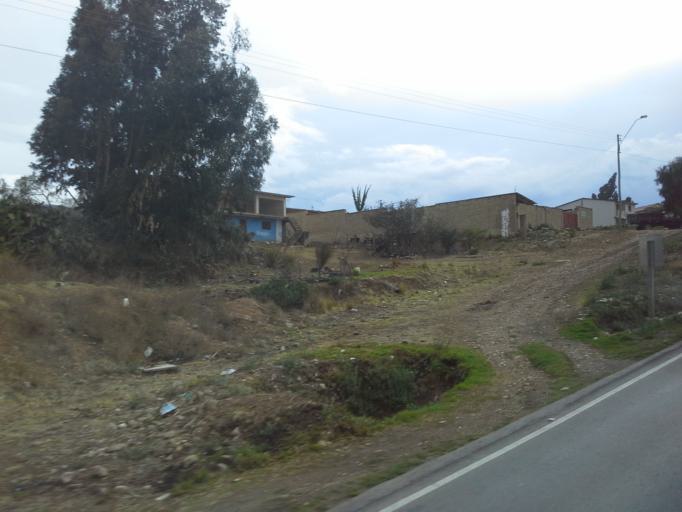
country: BO
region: Cochabamba
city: Colomi
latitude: -17.4158
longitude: -65.9599
